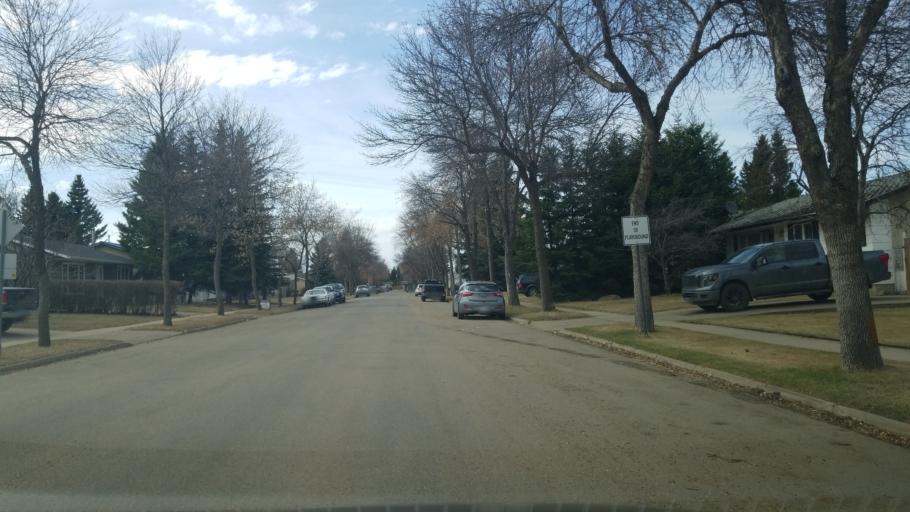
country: CA
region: Saskatchewan
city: Lloydminster
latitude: 53.2716
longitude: -109.9978
